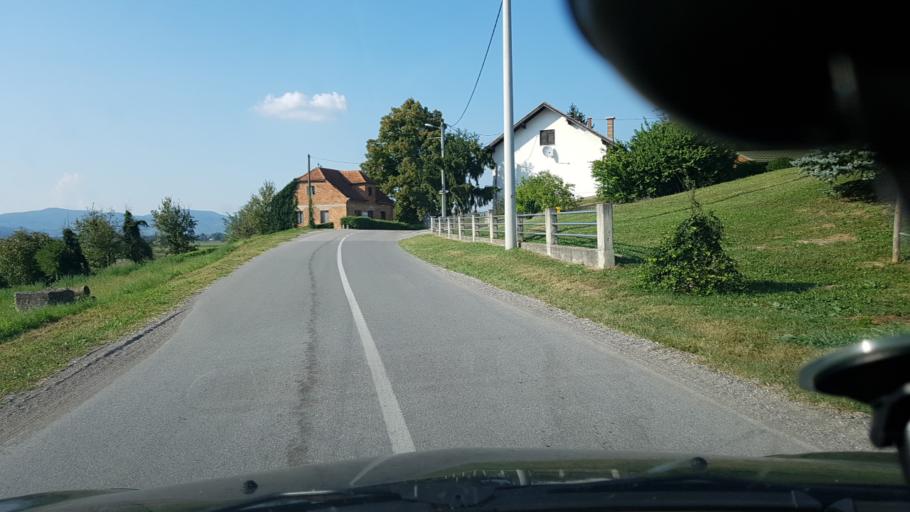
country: HR
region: Zagrebacka
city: Pojatno
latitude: 45.9384
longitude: 15.7277
